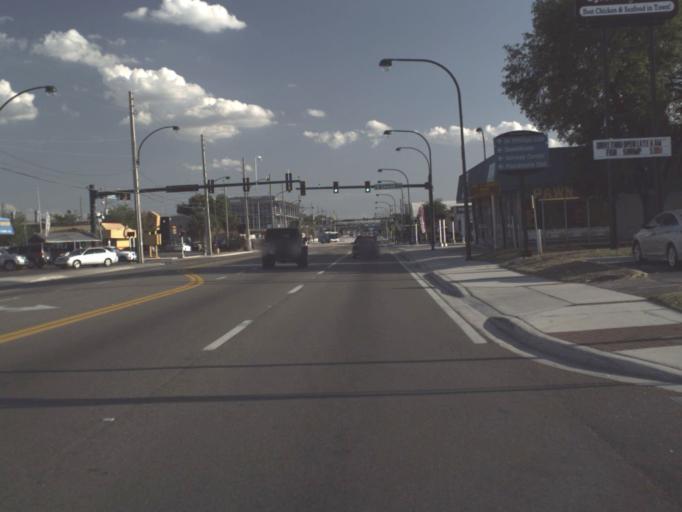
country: US
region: Florida
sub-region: Orange County
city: Orlando
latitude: 28.5411
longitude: -81.3973
